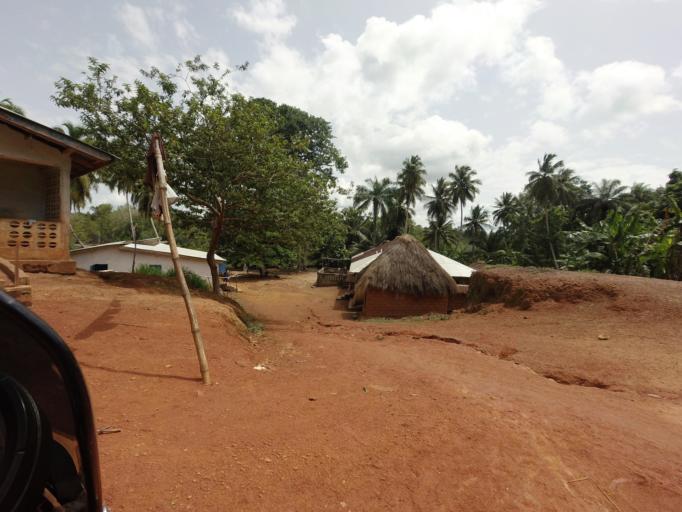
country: SL
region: Northern Province
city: Kambia
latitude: 9.0522
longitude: -12.9929
